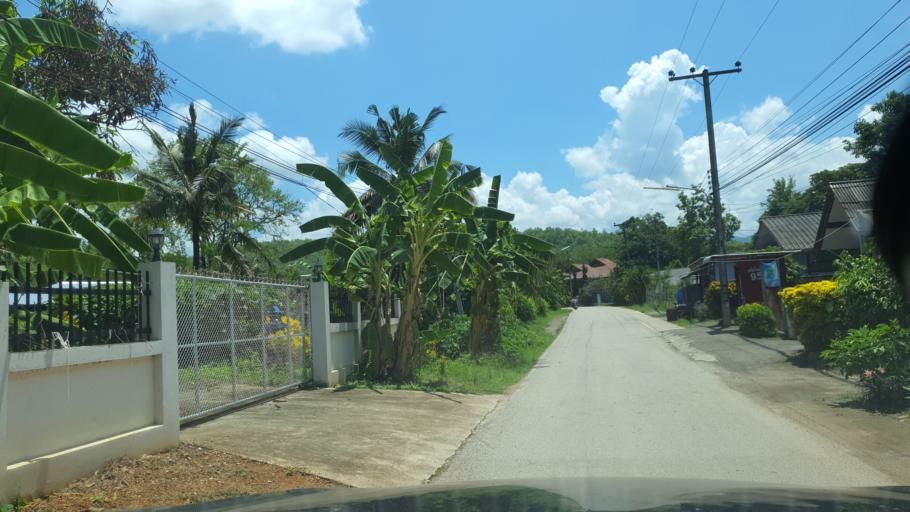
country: TH
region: Chiang Mai
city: Mae On
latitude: 18.8138
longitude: 99.2580
